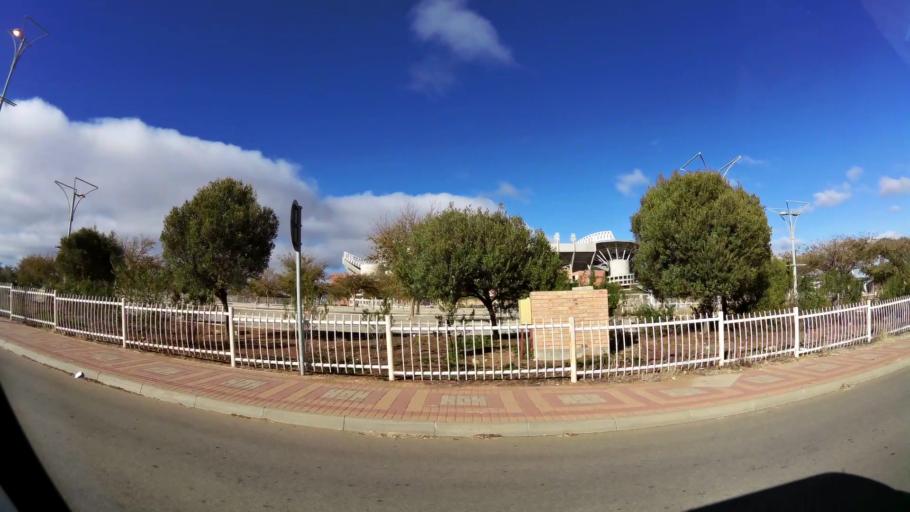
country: ZA
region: Limpopo
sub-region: Capricorn District Municipality
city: Polokwane
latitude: -23.9220
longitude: 29.4696
